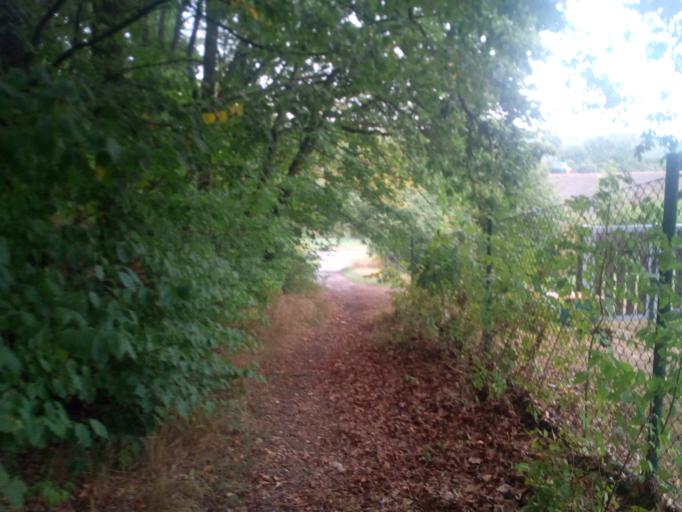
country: DE
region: Saxony
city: Kreischa
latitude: 50.9362
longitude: 13.7795
